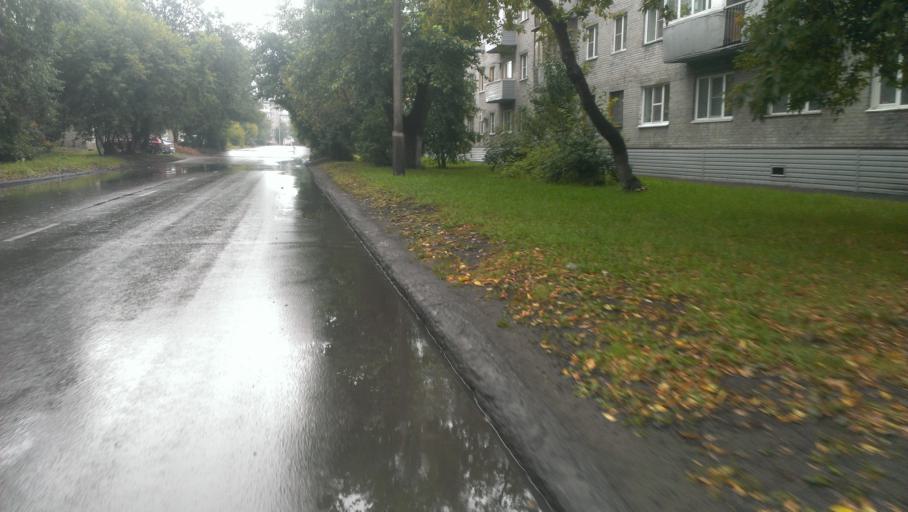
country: RU
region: Altai Krai
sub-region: Gorod Barnaulskiy
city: Barnaul
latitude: 53.3591
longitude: 83.7628
